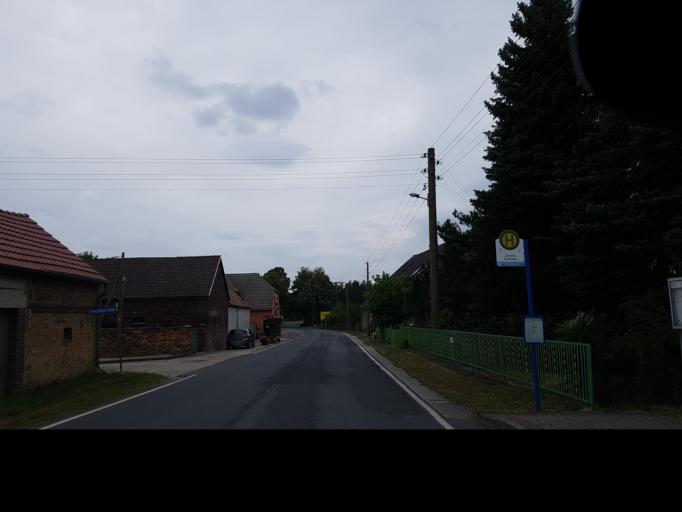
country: DE
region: Brandenburg
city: Sallgast
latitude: 51.6089
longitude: 13.8443
